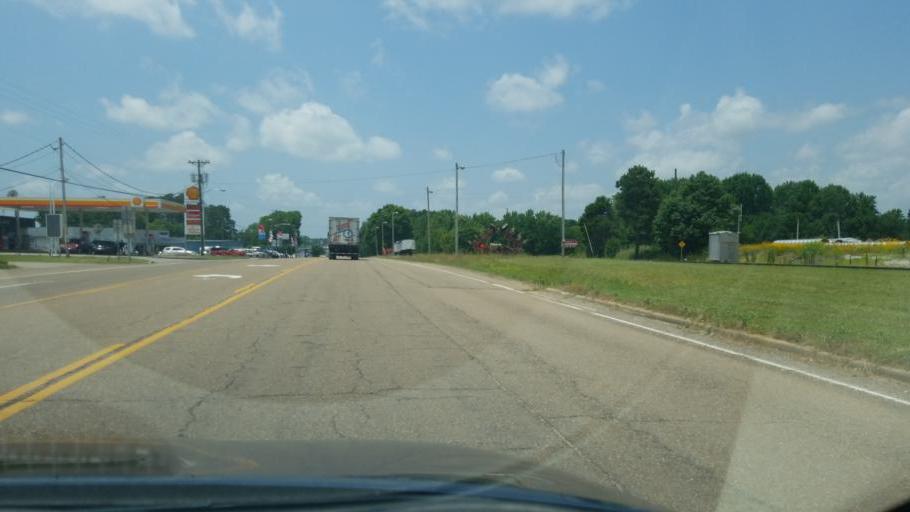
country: US
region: Tennessee
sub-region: Carroll County
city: Huntingdon
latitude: 36.0101
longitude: -88.3982
